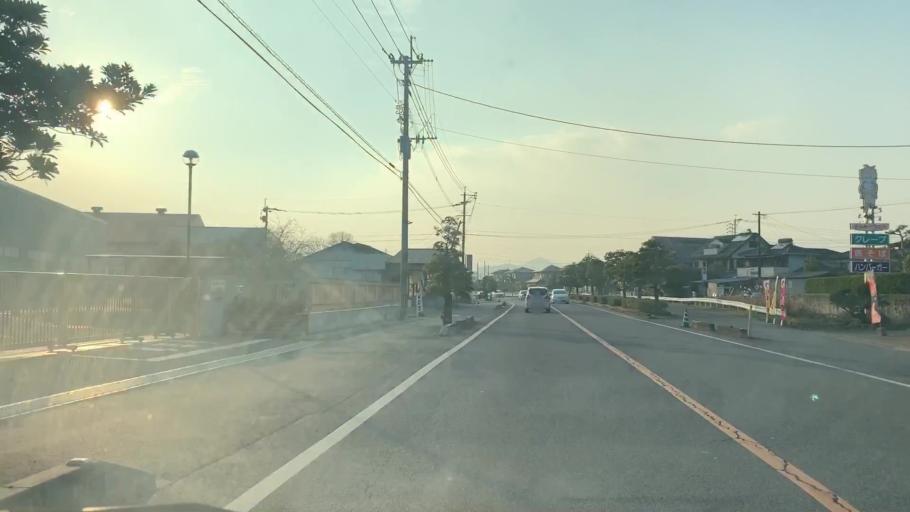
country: JP
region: Saga Prefecture
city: Saga-shi
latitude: 33.2805
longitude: 130.1546
